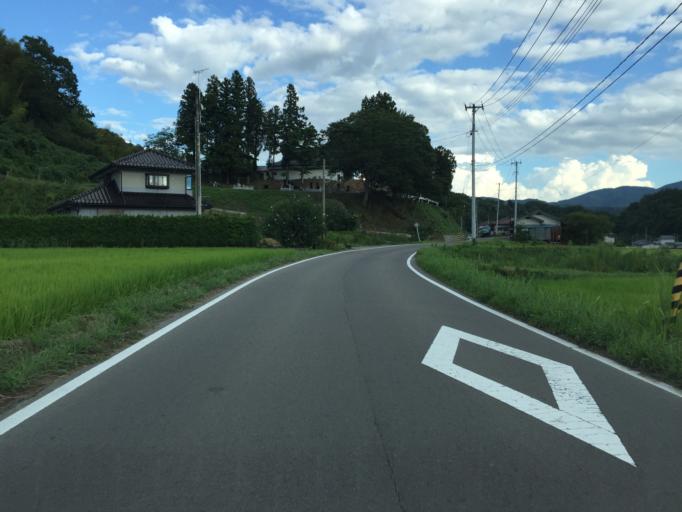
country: JP
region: Fukushima
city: Fukushima-shi
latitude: 37.6760
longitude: 140.5835
